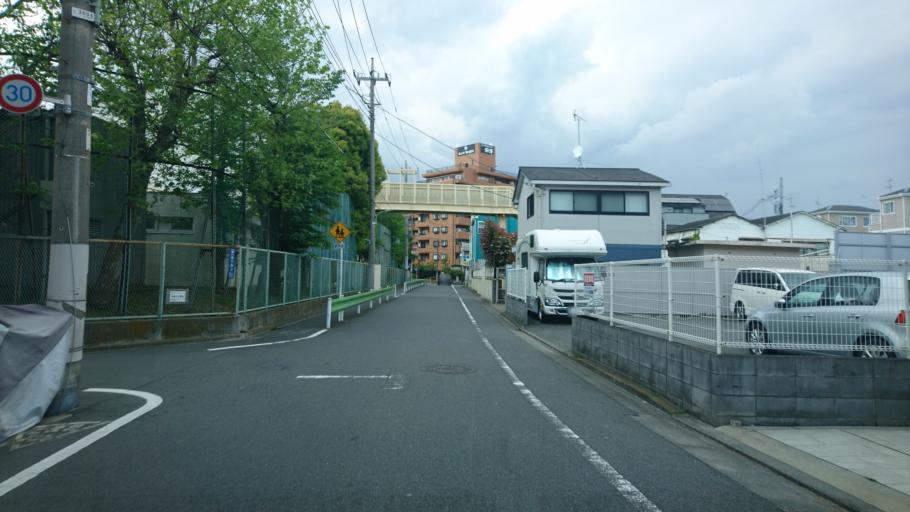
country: JP
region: Kanagawa
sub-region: Kawasaki-shi
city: Kawasaki
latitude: 35.5454
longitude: 139.7174
